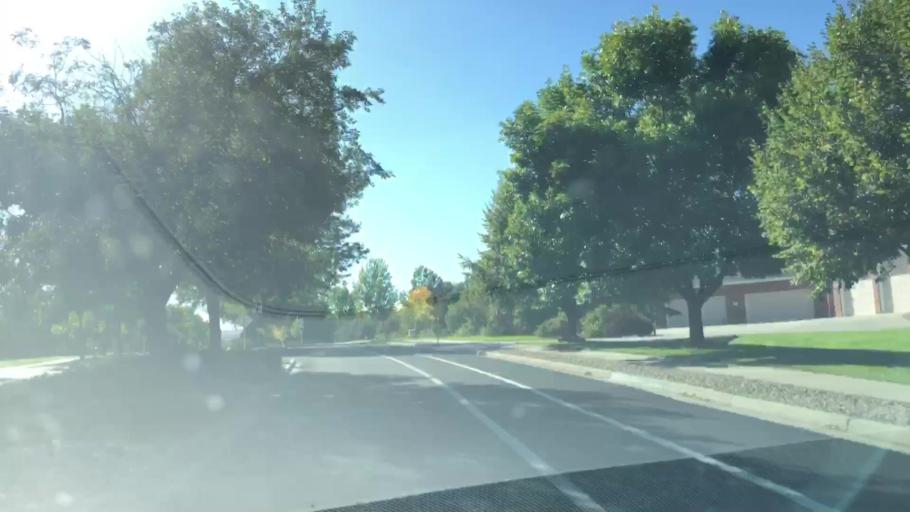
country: US
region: Colorado
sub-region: Larimer County
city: Loveland
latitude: 40.4879
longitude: -105.0601
